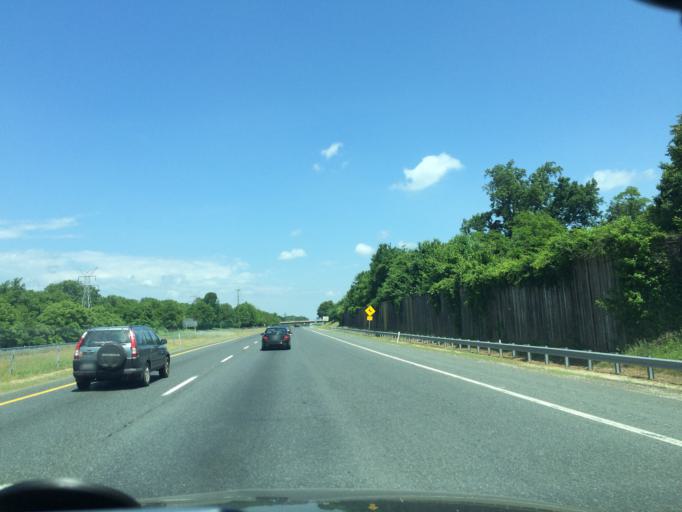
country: US
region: Maryland
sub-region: Baltimore County
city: Reisterstown
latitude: 39.4457
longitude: -76.8267
